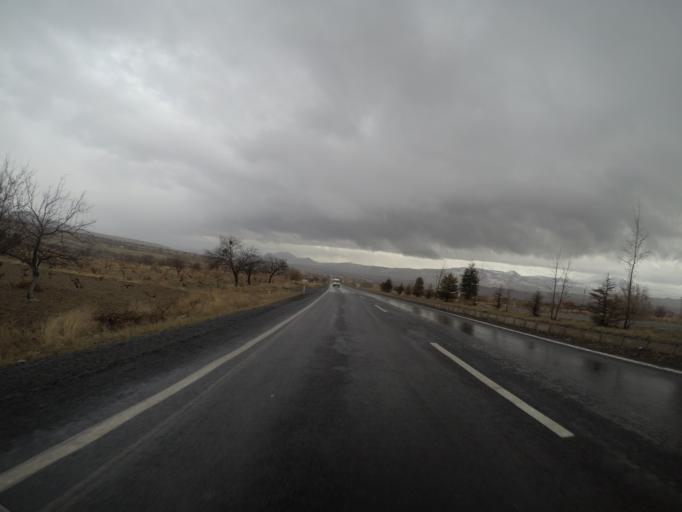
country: TR
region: Kayseri
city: Incesu
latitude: 38.6811
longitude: 35.2038
